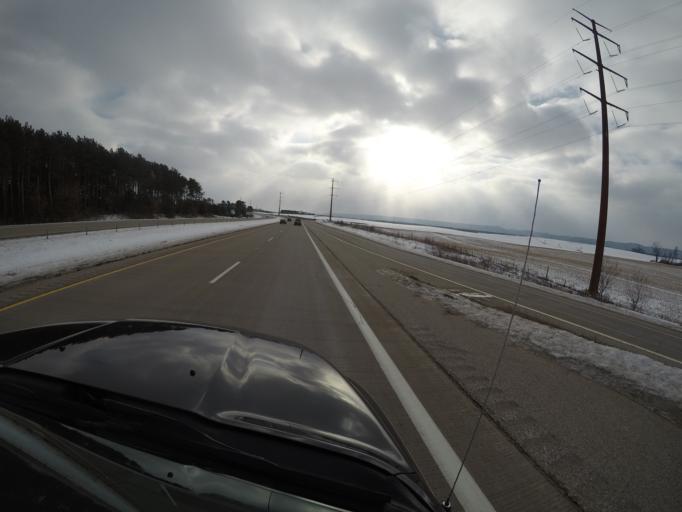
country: US
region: Wisconsin
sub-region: La Crosse County
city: Holmen
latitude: 43.9662
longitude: -91.2864
